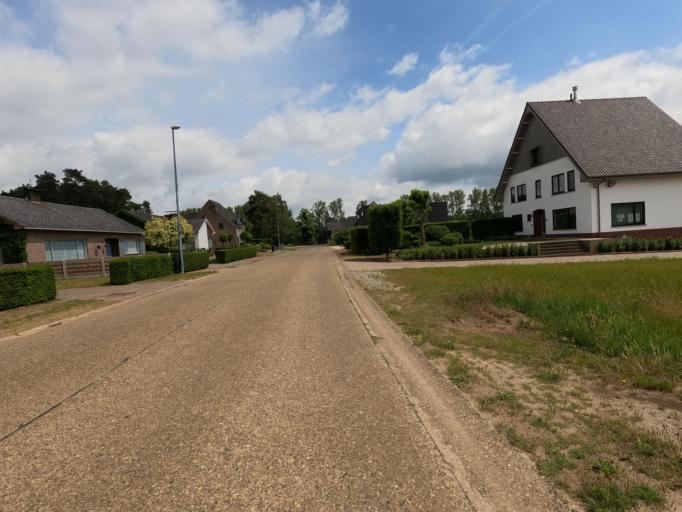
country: BE
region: Flanders
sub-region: Provincie Antwerpen
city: Vorselaar
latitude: 51.2057
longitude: 4.7902
